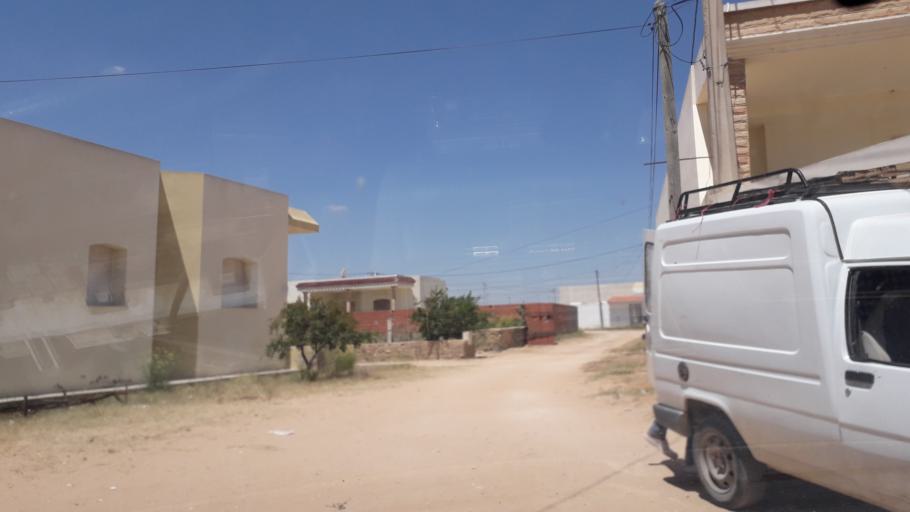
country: TN
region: Safaqis
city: Al Qarmadah
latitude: 34.8312
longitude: 10.7726
